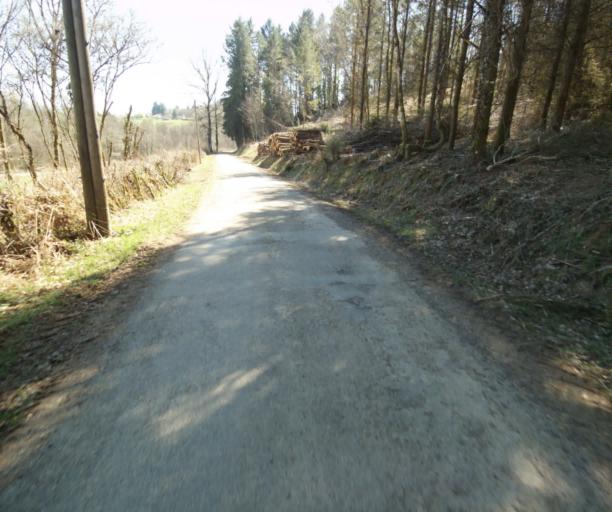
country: FR
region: Limousin
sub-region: Departement de la Correze
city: Saint-Clement
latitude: 45.3248
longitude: 1.7030
